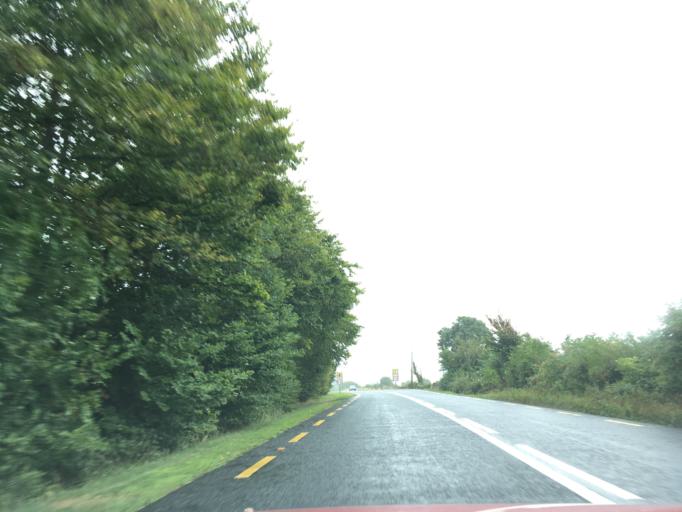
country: IE
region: Munster
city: Carrick-on-Suir
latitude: 52.3519
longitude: -7.4662
